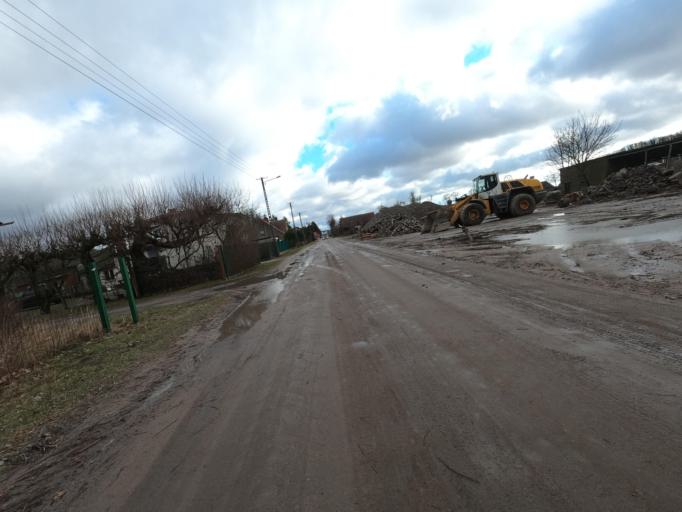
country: PL
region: Greater Poland Voivodeship
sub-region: Powiat pilski
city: Miasteczko Krajenskie
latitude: 53.1116
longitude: 17.0058
